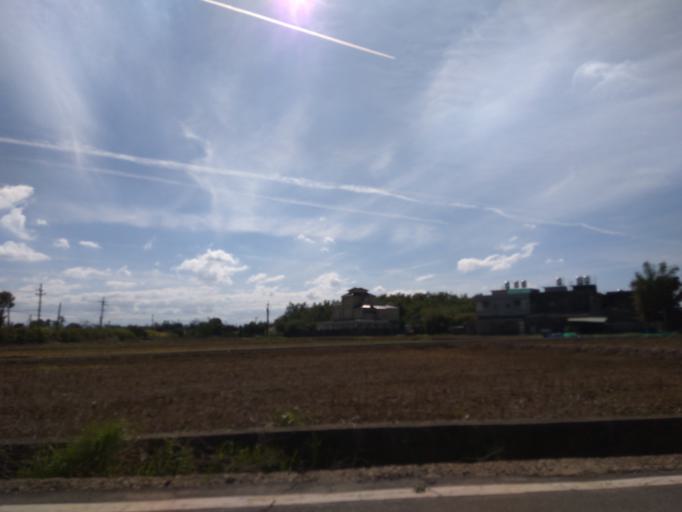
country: TW
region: Taiwan
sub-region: Hsinchu
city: Zhubei
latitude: 25.0120
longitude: 121.0881
